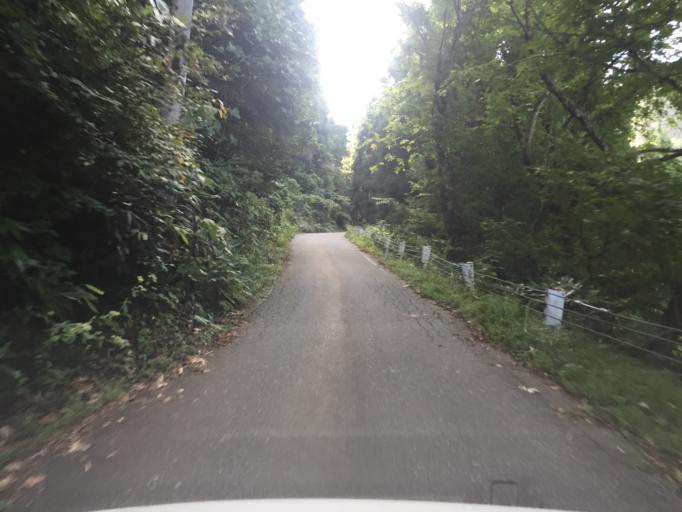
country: JP
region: Fukushima
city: Inawashiro
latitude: 37.4322
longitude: 139.9772
